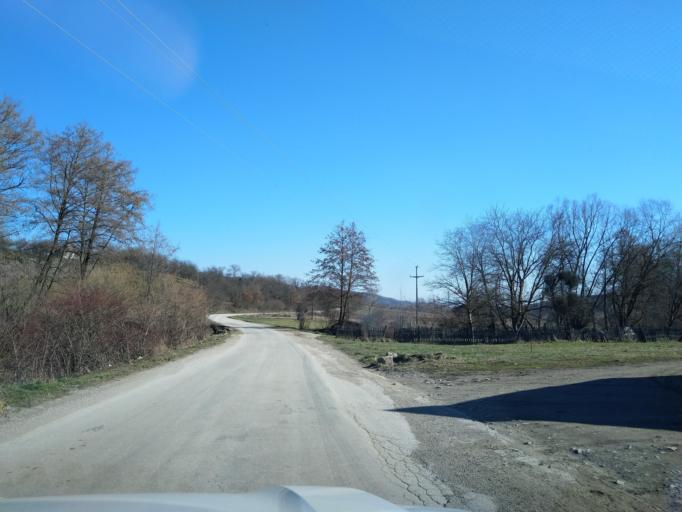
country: RS
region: Central Serbia
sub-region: Zlatiborski Okrug
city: Kosjeric
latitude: 43.9386
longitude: 19.8770
